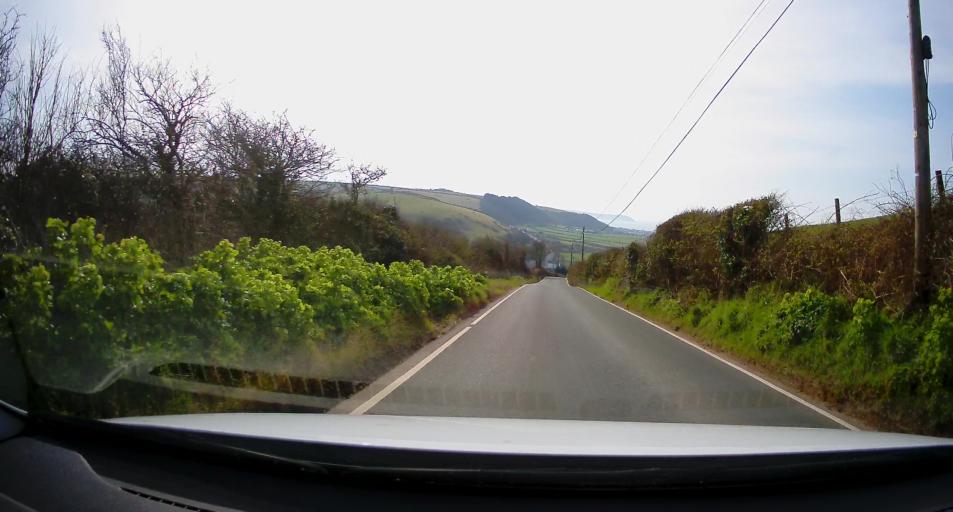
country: GB
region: Wales
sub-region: County of Ceredigion
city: Aberaeron
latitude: 52.2533
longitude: -4.2225
